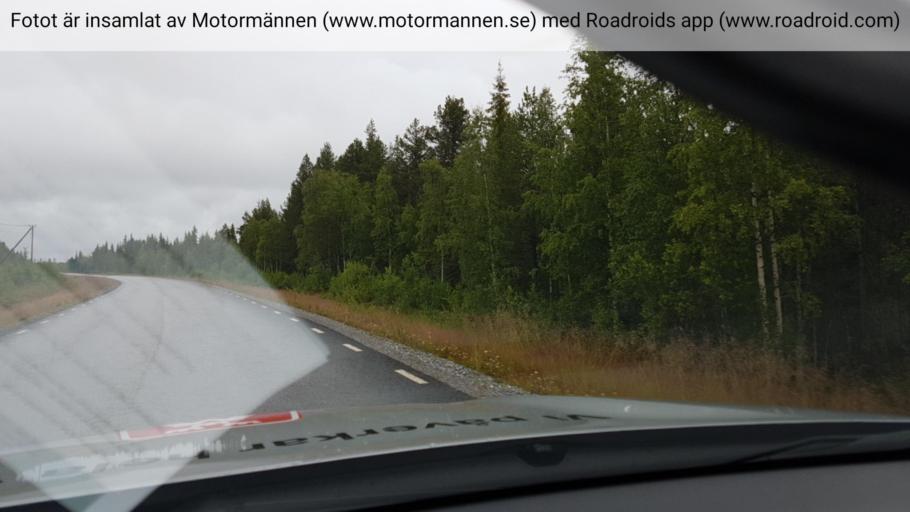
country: SE
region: Norrbotten
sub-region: Gallivare Kommun
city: Gaellivare
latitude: 66.7770
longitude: 21.0516
